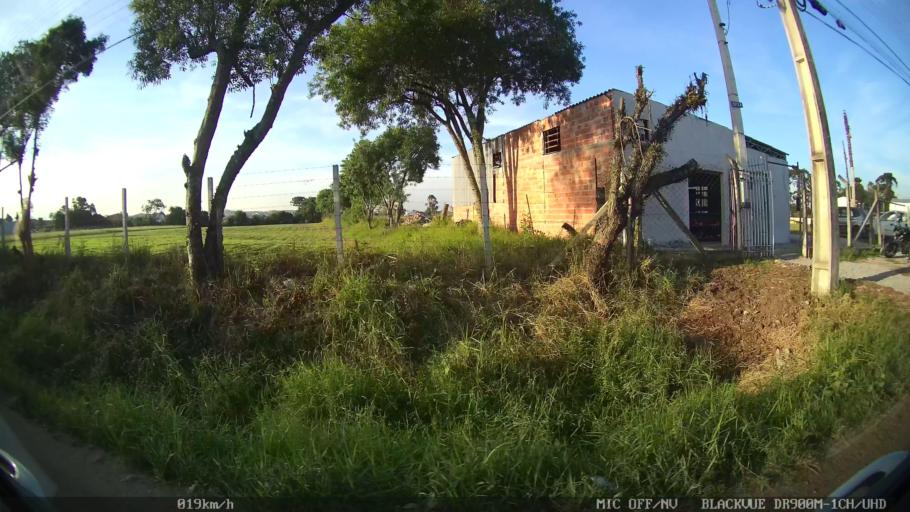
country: BR
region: Parana
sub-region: Pinhais
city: Pinhais
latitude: -25.4608
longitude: -49.1555
